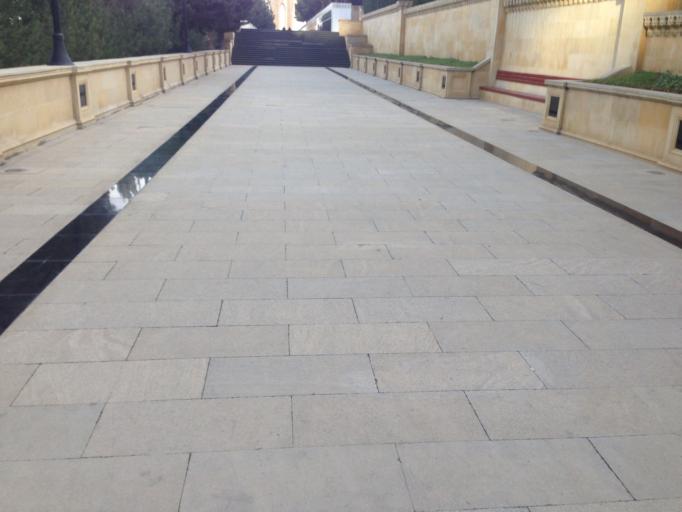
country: AZ
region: Baki
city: Badamdar
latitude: 40.3572
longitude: 49.8279
